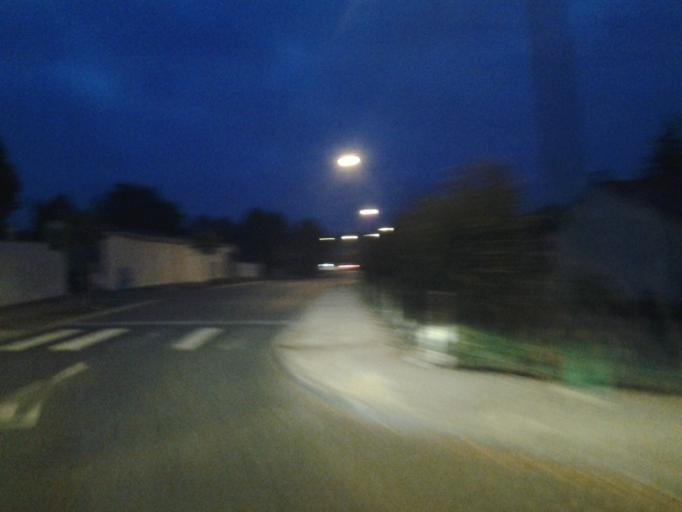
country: FR
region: Pays de la Loire
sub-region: Departement de la Vendee
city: Landeronde
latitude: 46.6560
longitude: -1.5655
